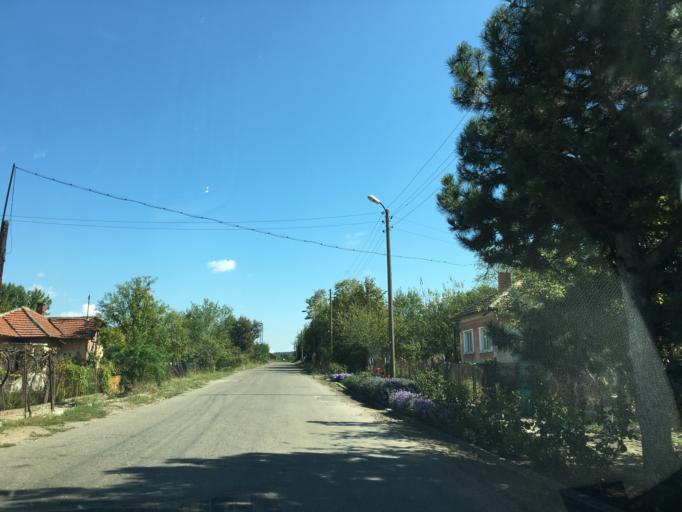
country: BG
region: Montana
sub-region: Obshtina Brusartsi
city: Brusartsi
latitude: 43.7651
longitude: 23.0429
